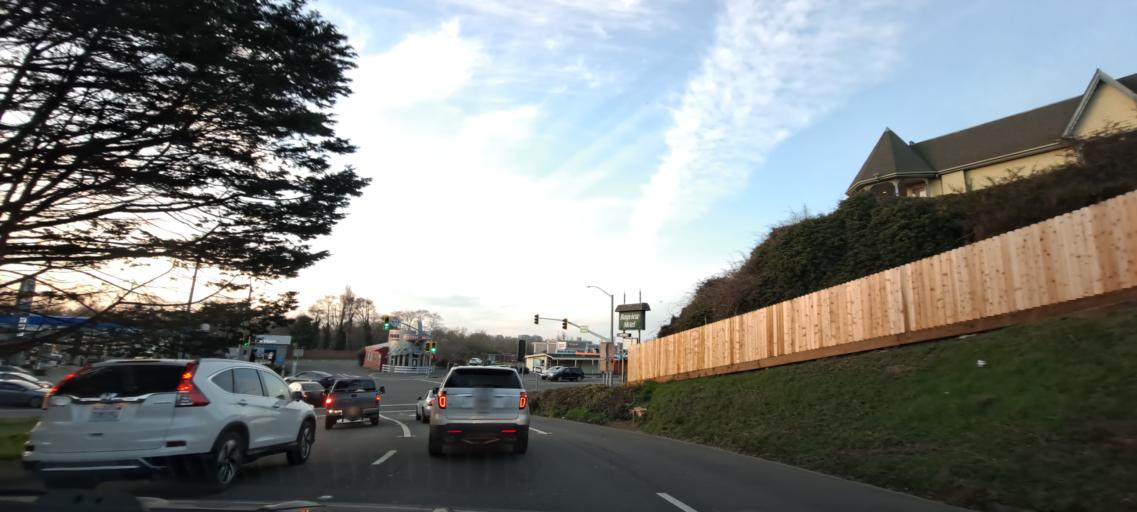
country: US
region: California
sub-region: Humboldt County
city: Bayview
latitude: 40.7829
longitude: -124.1831
